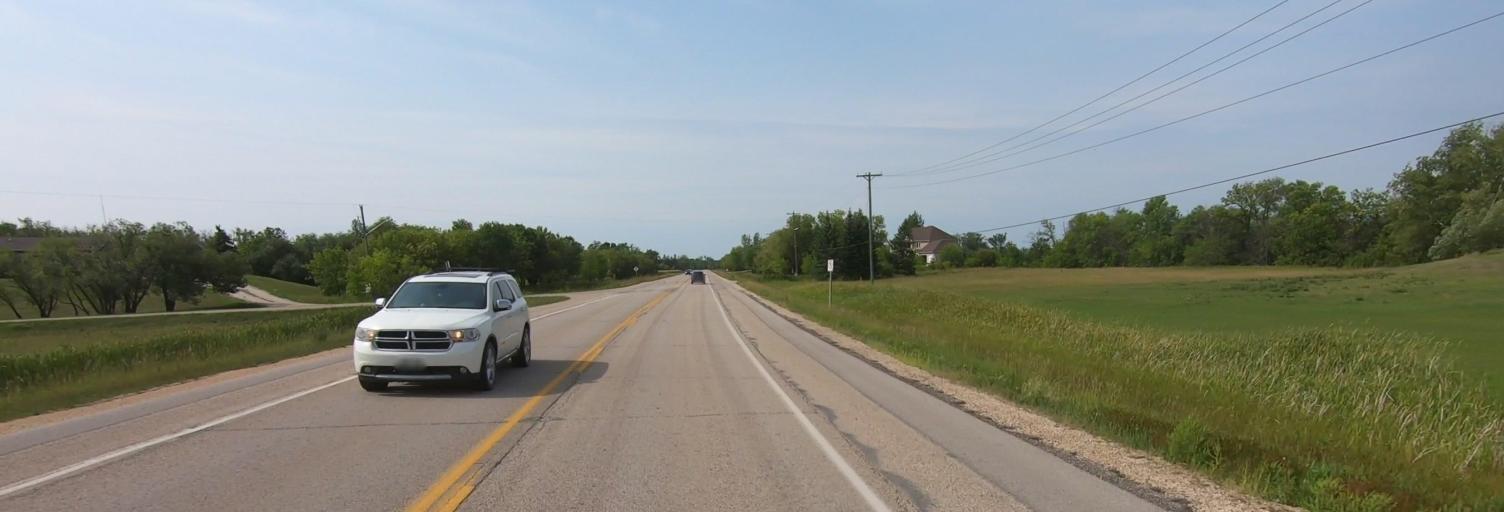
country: CA
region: Manitoba
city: Niverville
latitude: 49.6949
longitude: -97.1004
